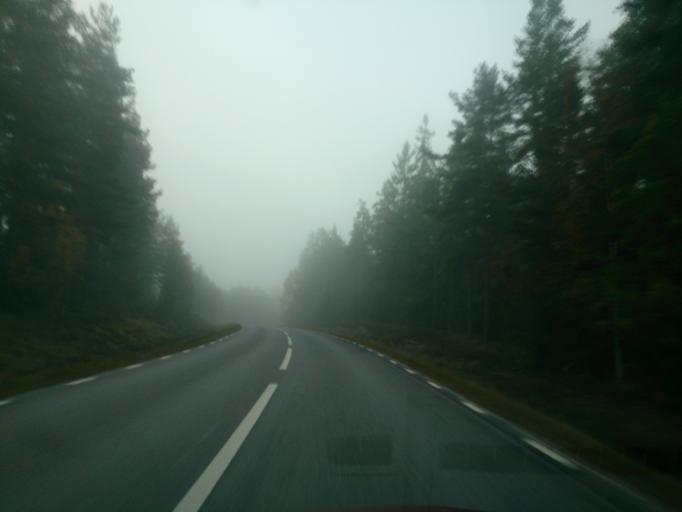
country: SE
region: OEstergoetland
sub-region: Atvidabergs Kommun
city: Atvidaberg
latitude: 58.1314
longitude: 15.9555
